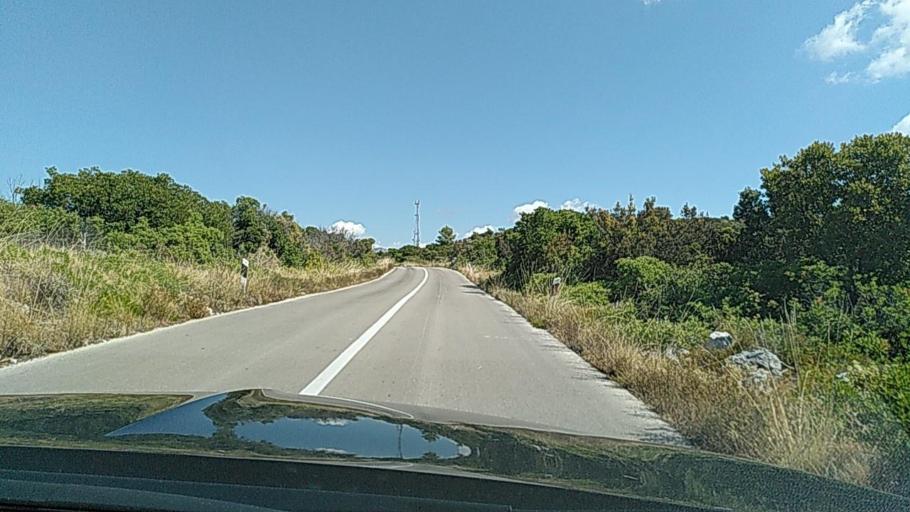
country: HR
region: Dubrovacko-Neretvanska
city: Orebic
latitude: 43.1258
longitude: 17.1229
